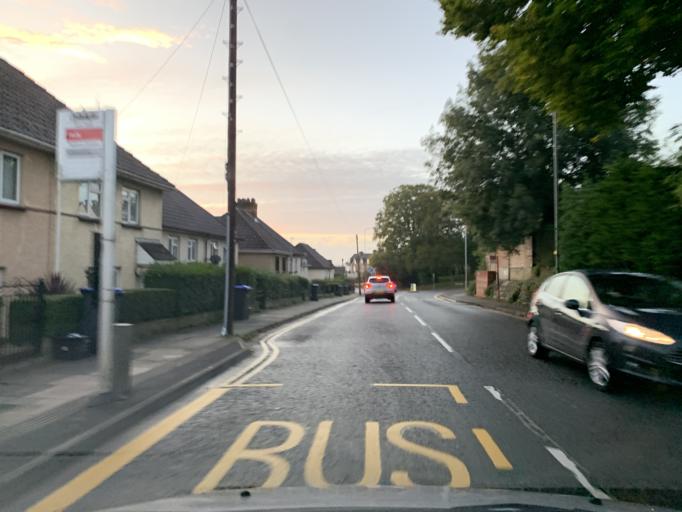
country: GB
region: England
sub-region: Wiltshire
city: Salisbury
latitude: 51.0779
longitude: -1.8125
